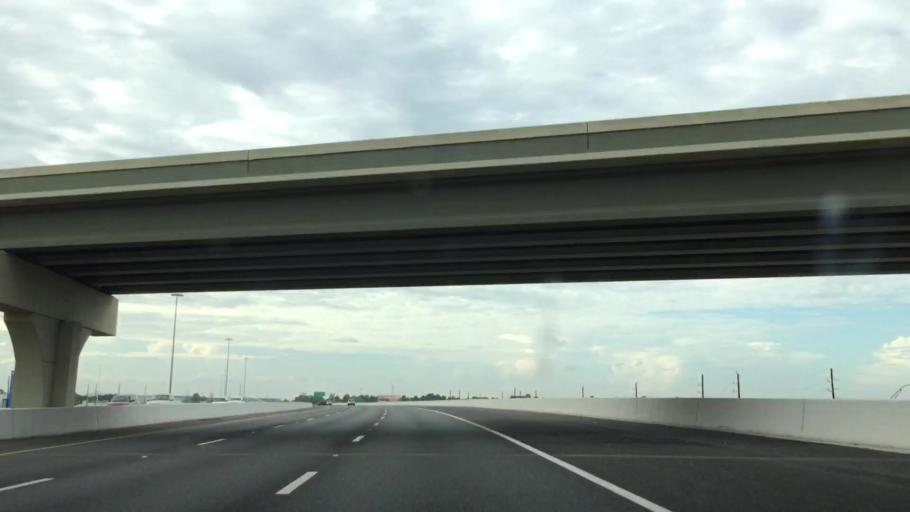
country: US
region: Texas
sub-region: Harris County
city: Tomball
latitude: 30.0522
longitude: -95.6137
